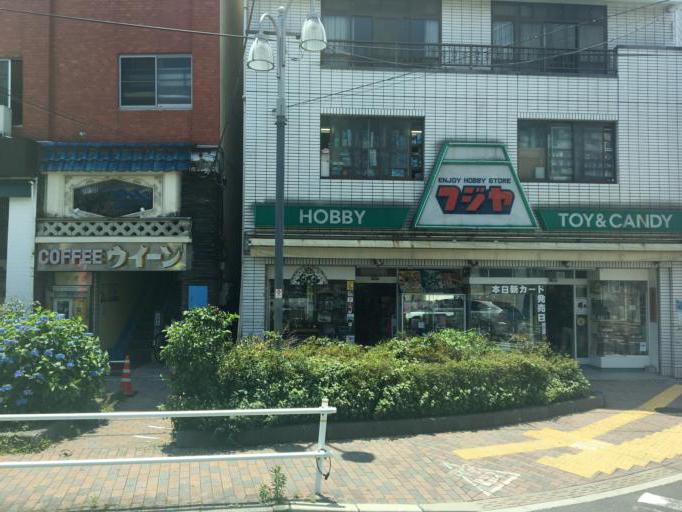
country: JP
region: Saitama
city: Kawaguchi
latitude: 35.7633
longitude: 139.6901
